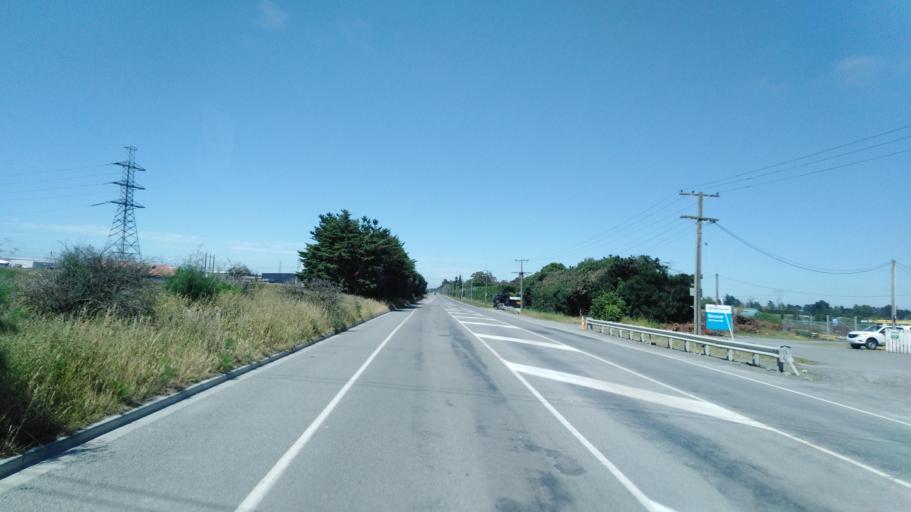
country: NZ
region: Canterbury
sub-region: Selwyn District
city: Prebbleton
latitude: -43.5284
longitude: 172.4997
